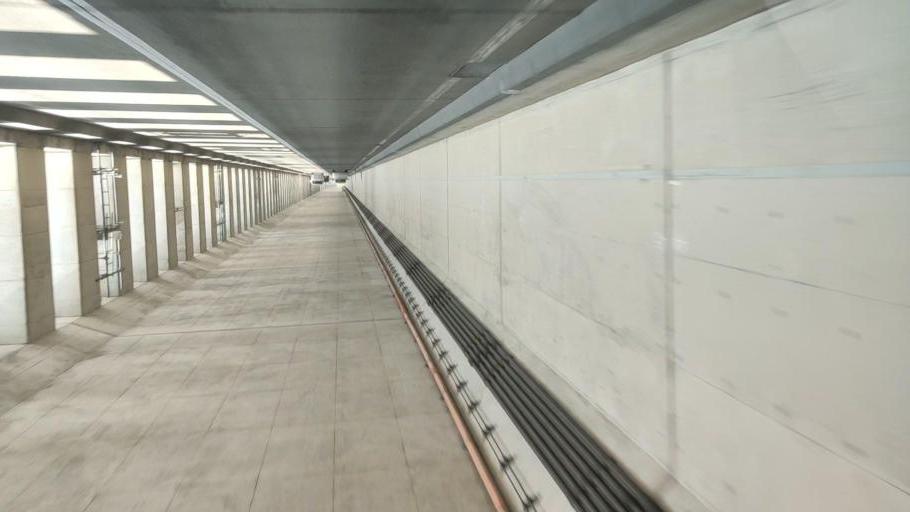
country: JP
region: Hokkaido
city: Rumoi
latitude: 43.6717
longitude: 141.3479
